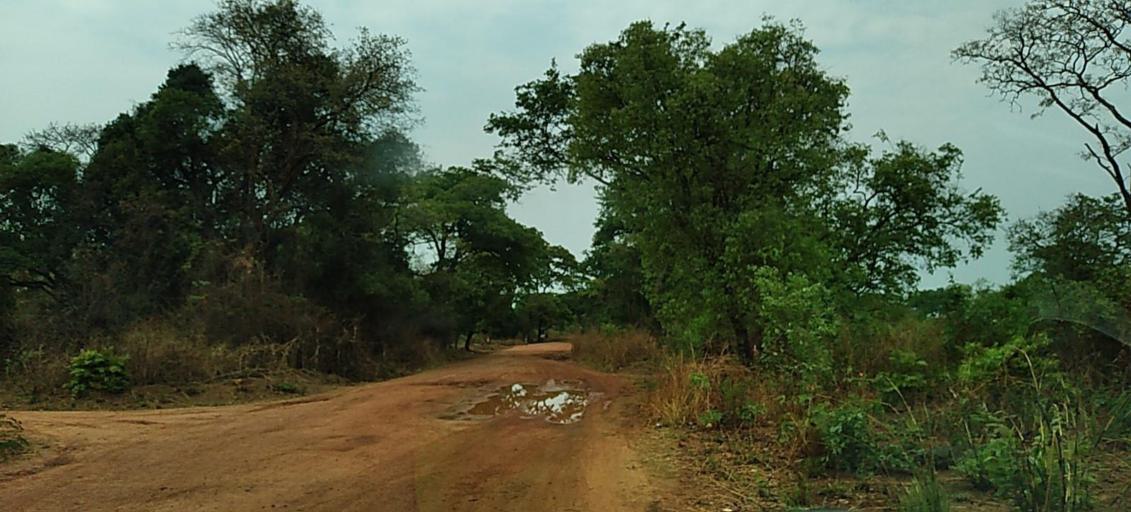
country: ZM
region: North-Western
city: Solwezi
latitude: -12.3467
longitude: 26.5298
